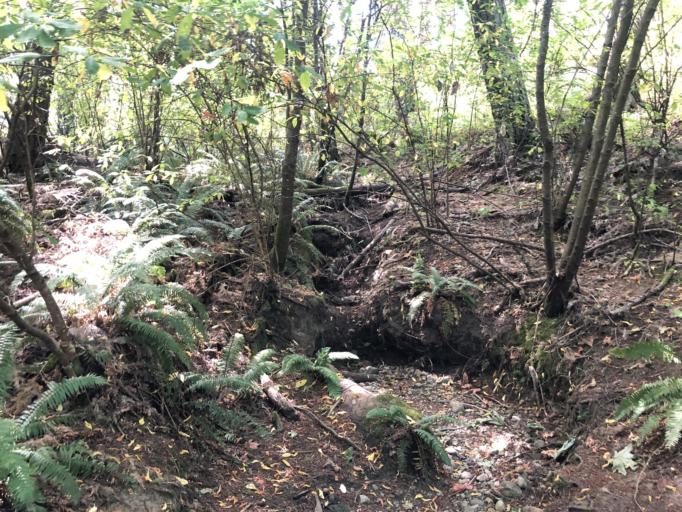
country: CA
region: British Columbia
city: Metchosin
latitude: 48.3638
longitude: -123.5372
